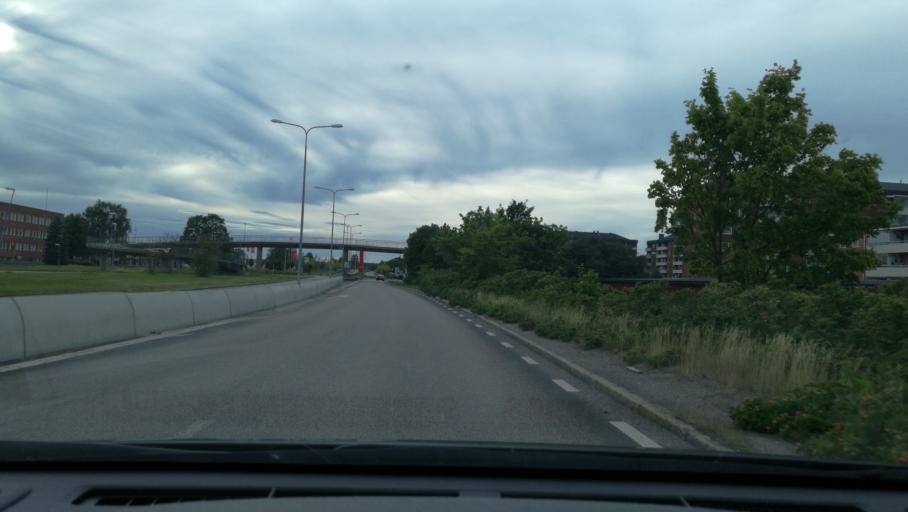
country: SE
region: Vaestmanland
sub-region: Kopings Kommun
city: Koping
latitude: 59.5097
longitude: 15.9915
